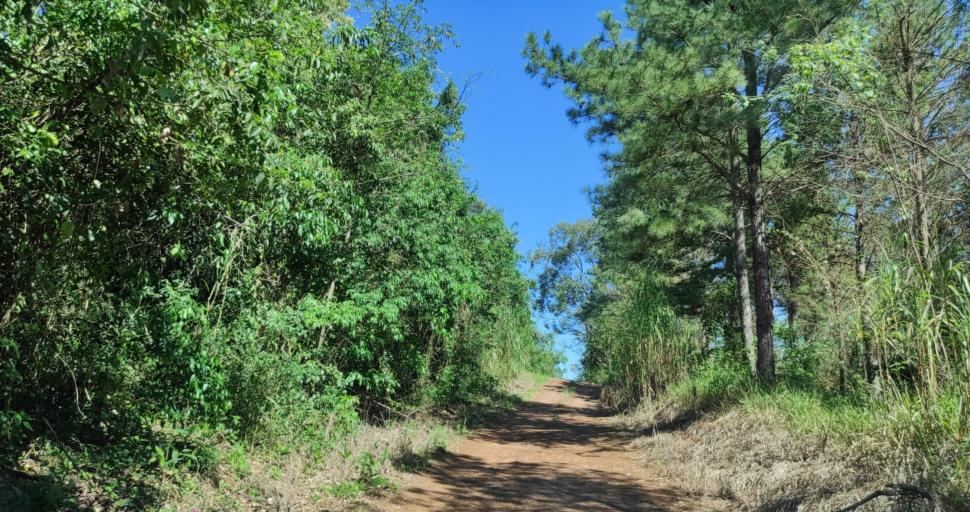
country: AR
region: Misiones
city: Ruiz de Montoya
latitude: -26.9474
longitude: -54.9808
